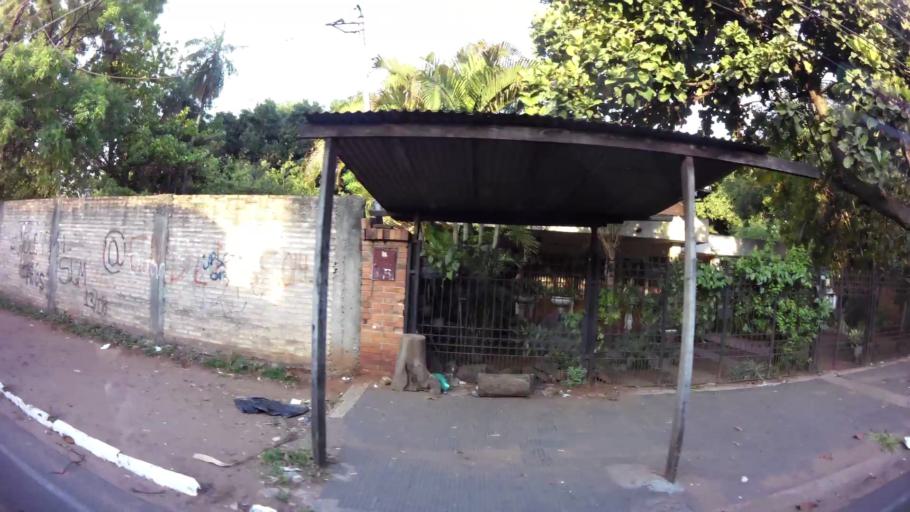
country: PY
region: Central
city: San Lorenzo
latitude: -25.3473
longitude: -57.5037
